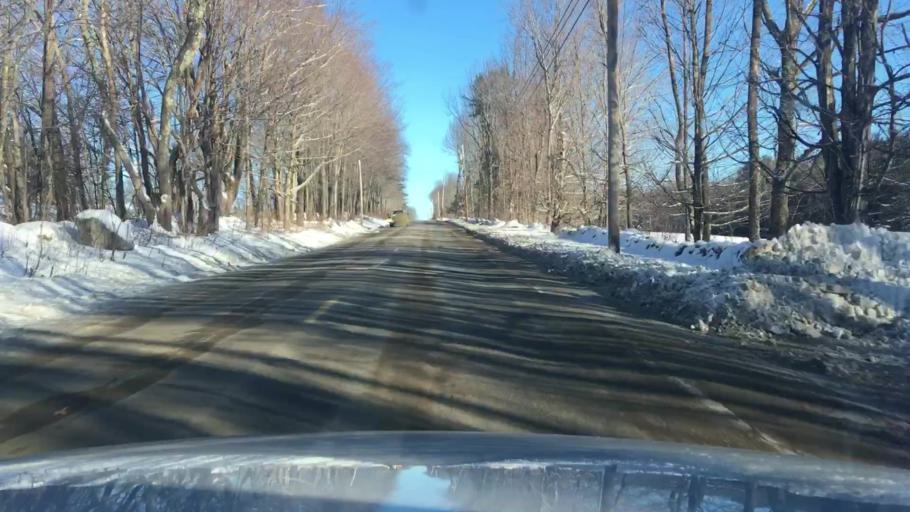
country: US
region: Maine
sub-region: Kennebec County
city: Mount Vernon
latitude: 44.4763
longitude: -69.9726
